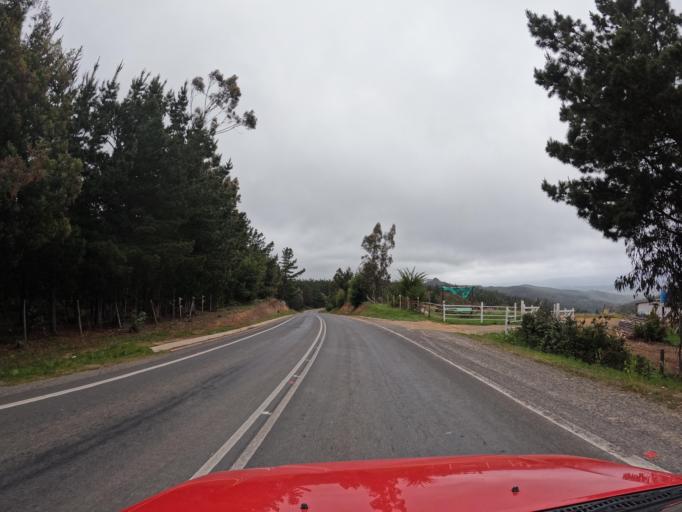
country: CL
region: O'Higgins
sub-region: Provincia de Colchagua
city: Santa Cruz
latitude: -34.5976
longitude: -72.0165
